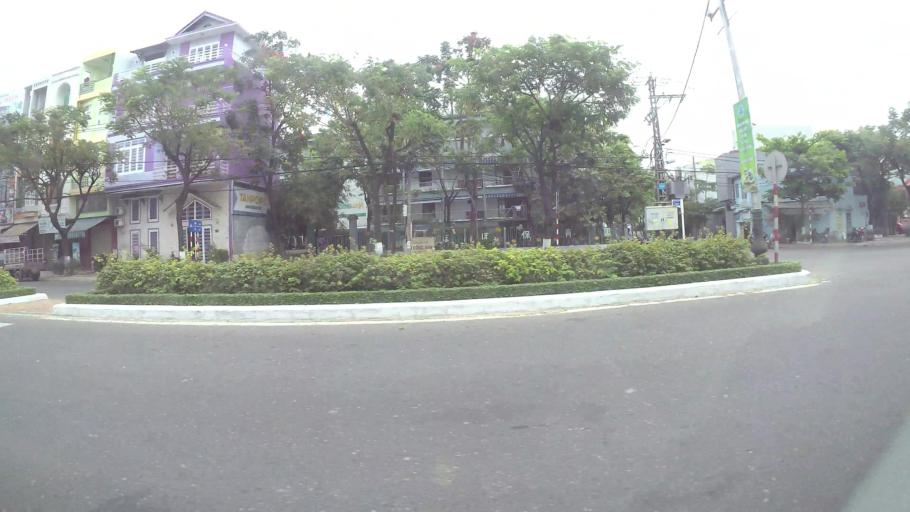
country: VN
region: Da Nang
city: Da Nang
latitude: 16.0839
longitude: 108.2216
